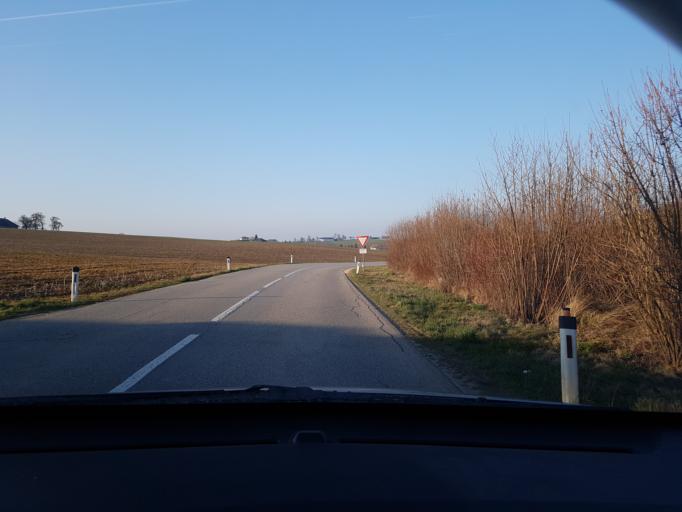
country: AT
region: Upper Austria
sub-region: Politischer Bezirk Steyr-Land
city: Sierning
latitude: 48.1269
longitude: 14.3272
